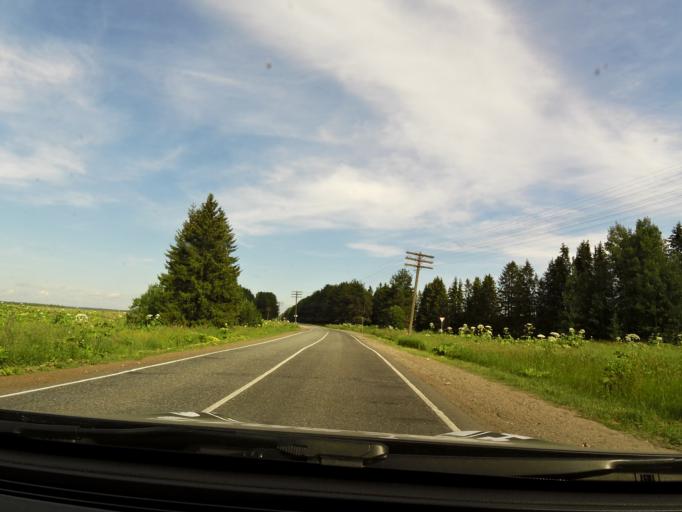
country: RU
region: Kirov
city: Slobodskoy
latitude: 58.7798
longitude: 50.4439
